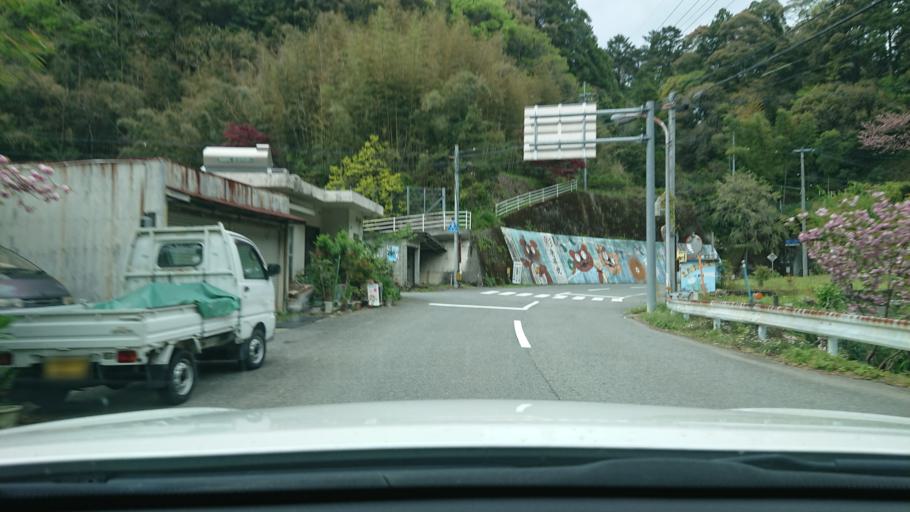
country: JP
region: Tokushima
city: Ishii
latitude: 33.9154
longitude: 134.4214
